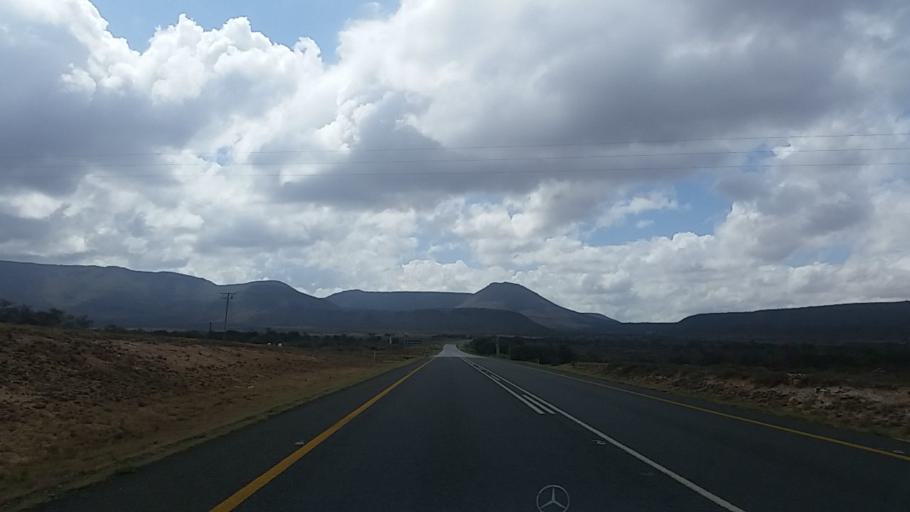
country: ZA
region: Eastern Cape
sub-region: Cacadu District Municipality
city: Graaff-Reinet
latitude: -32.0901
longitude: 24.6033
